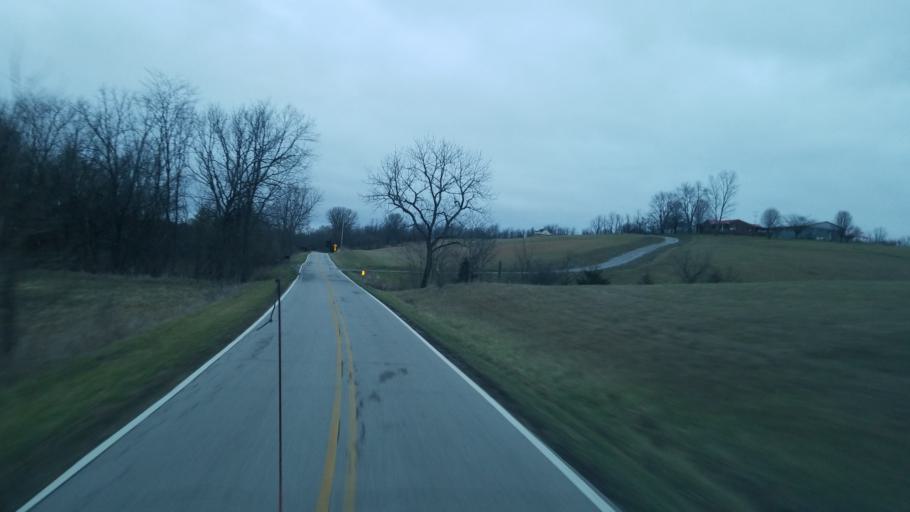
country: US
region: Kentucky
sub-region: Fleming County
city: Flemingsburg
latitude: 38.5190
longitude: -83.6964
